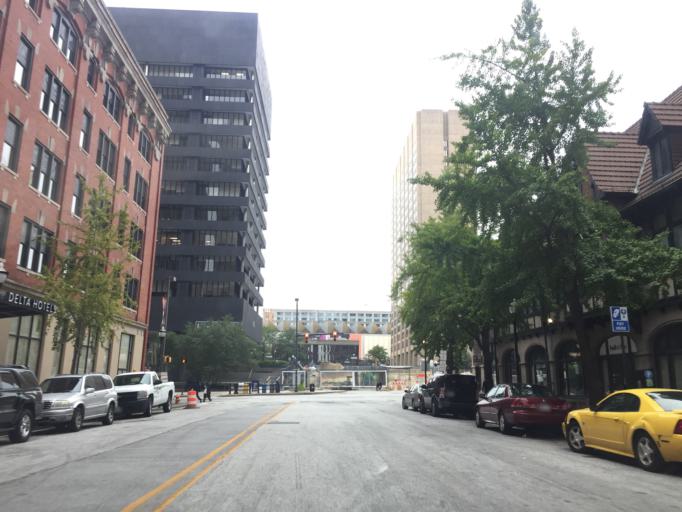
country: US
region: Maryland
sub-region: City of Baltimore
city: Baltimore
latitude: 39.2888
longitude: -76.6143
